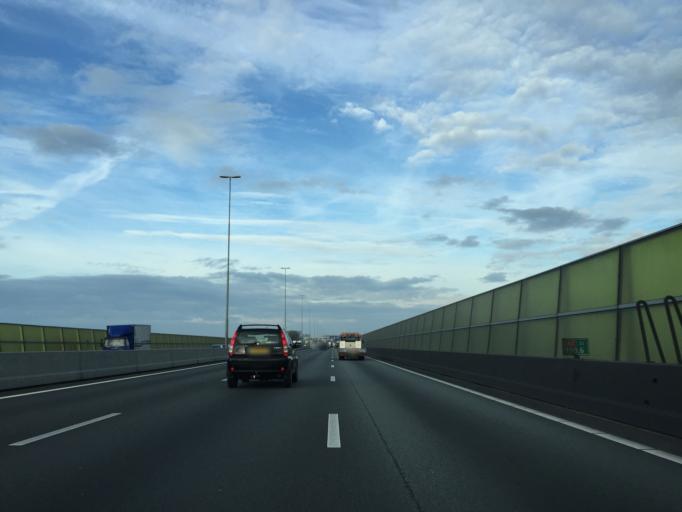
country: NL
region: Gelderland
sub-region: Gemeente Maasdriel
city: Hedel
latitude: 51.7409
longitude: 5.3020
